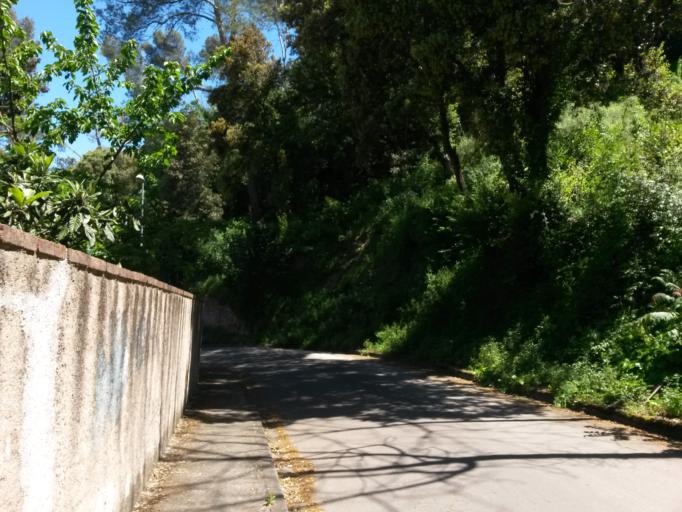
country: ES
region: Catalonia
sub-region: Provincia de Barcelona
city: Cerdanyola del Valles
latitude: 41.4816
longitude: 2.1337
